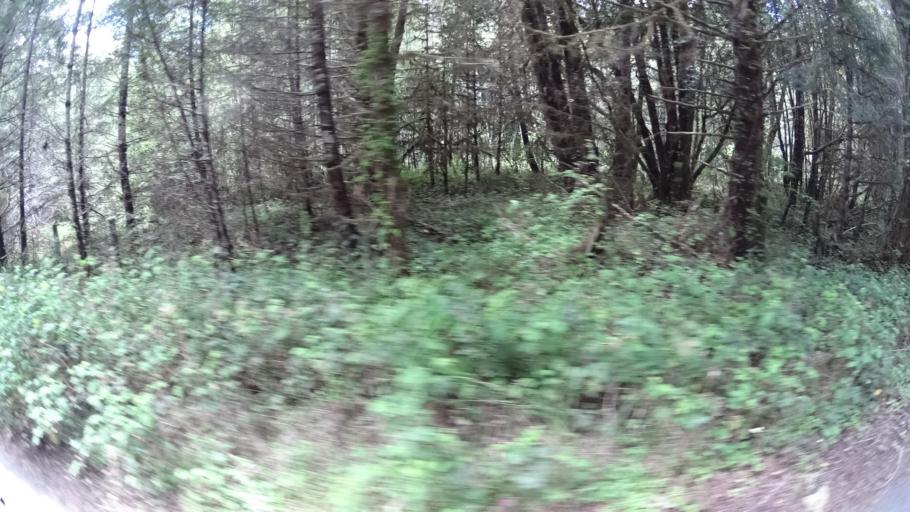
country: US
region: California
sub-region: Humboldt County
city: Blue Lake
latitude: 40.7807
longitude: -123.8775
